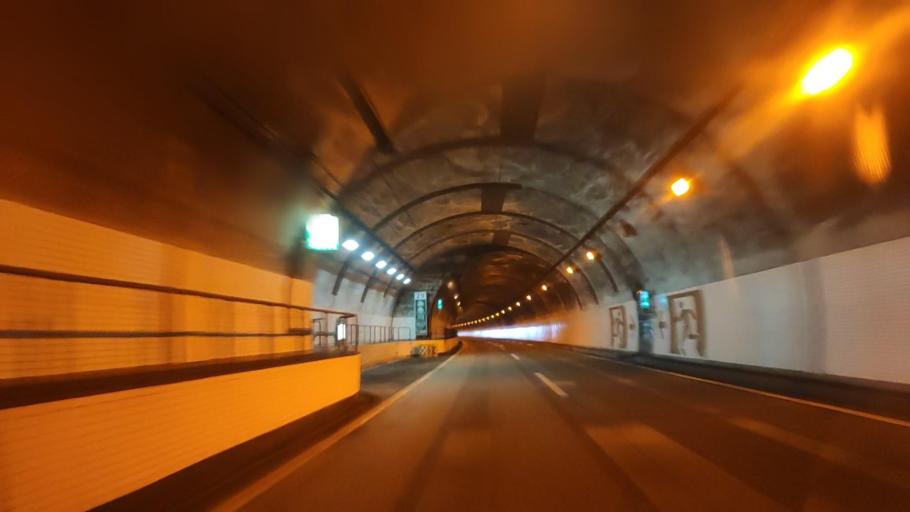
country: JP
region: Niigata
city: Itoigawa
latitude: 37.0195
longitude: 137.8382
